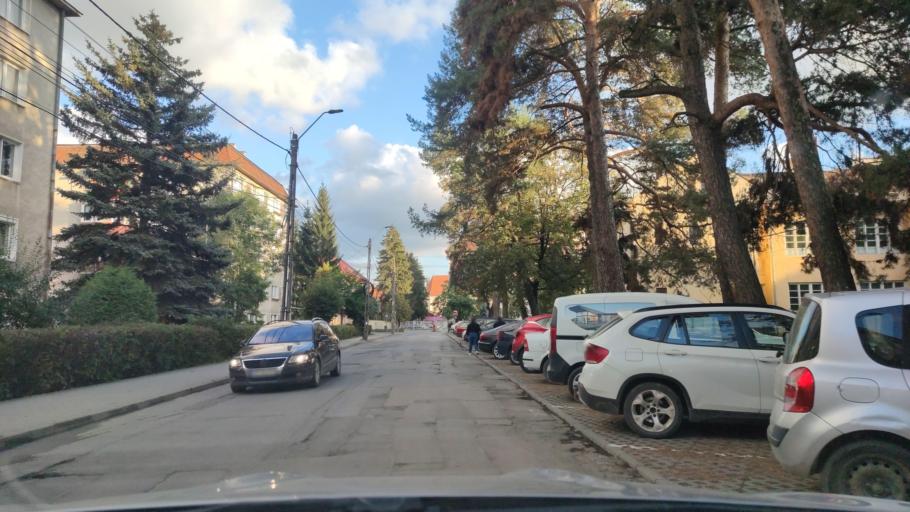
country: RO
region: Harghita
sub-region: Municipiul Gheorgheni
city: Gheorgheni
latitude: 46.7246
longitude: 25.6018
